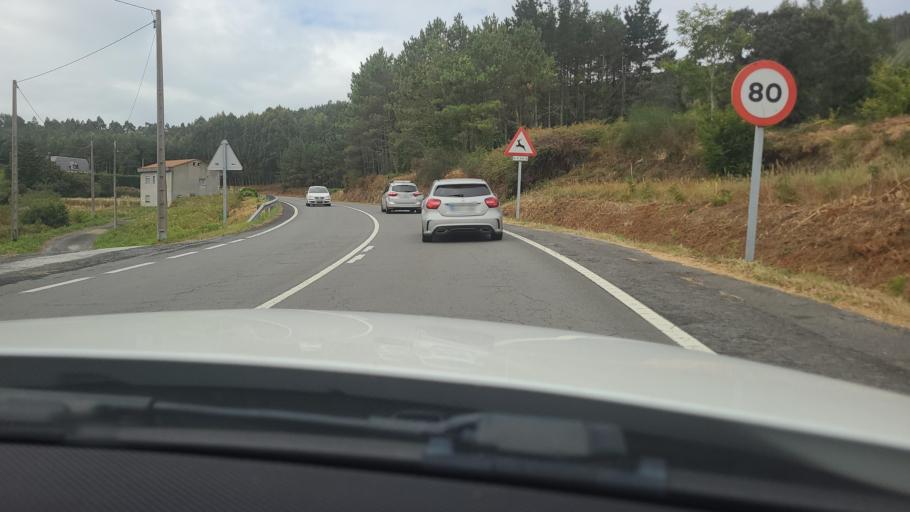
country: ES
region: Galicia
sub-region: Provincia da Coruna
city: Corcubion
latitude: 42.9396
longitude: -9.2358
